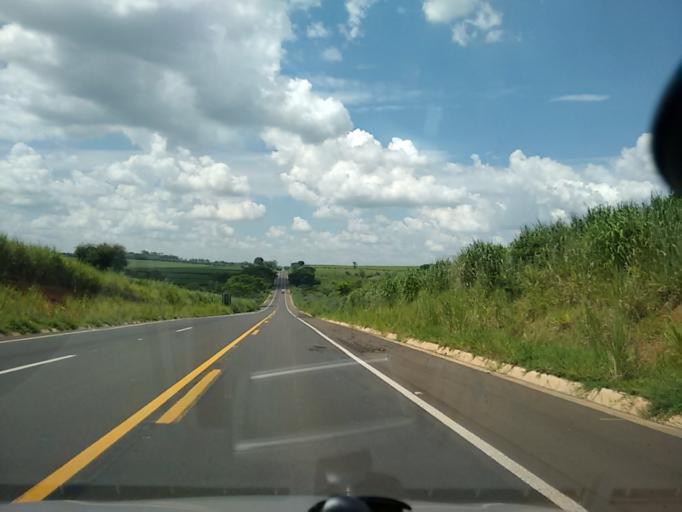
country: BR
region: Sao Paulo
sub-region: Osvaldo Cruz
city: Osvaldo Cruz
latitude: -21.8921
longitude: -50.8744
